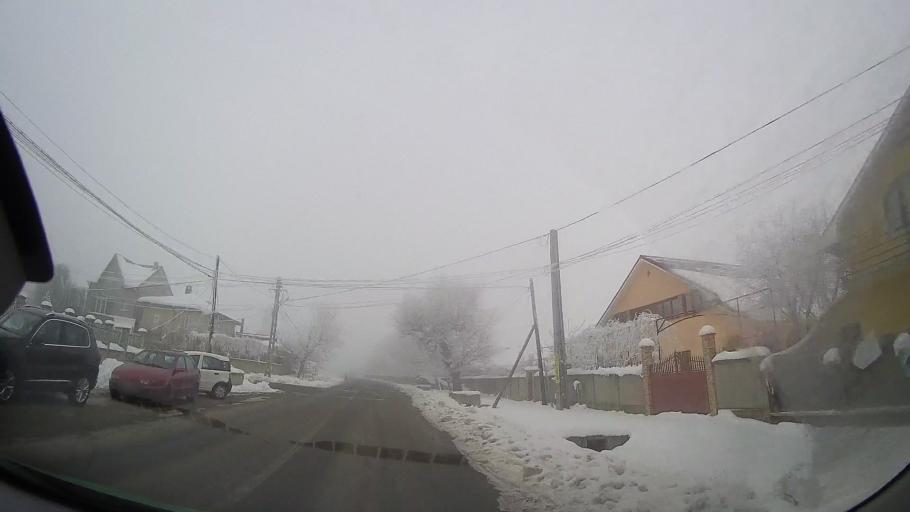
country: RO
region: Neamt
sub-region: Comuna Sabaoani
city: Sabaoani
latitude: 47.0235
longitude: 26.8632
